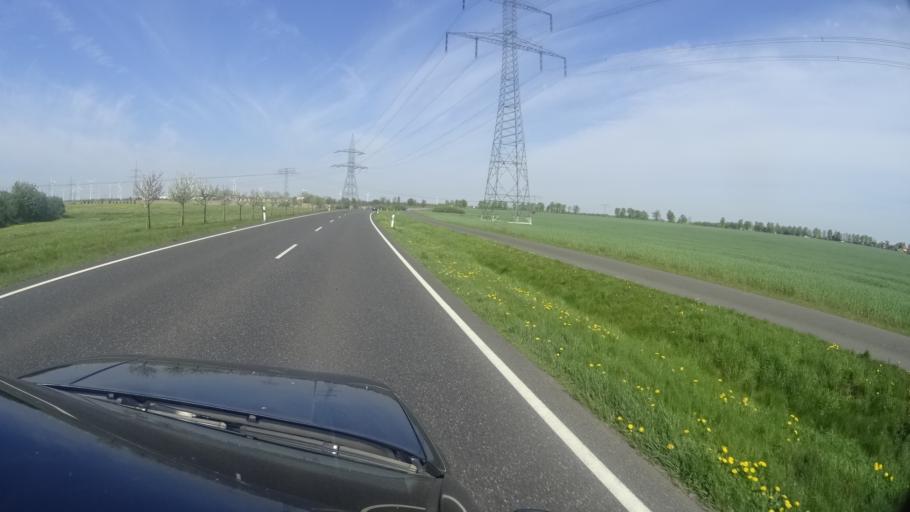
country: DE
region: Brandenburg
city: Nauen
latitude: 52.5955
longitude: 12.8594
